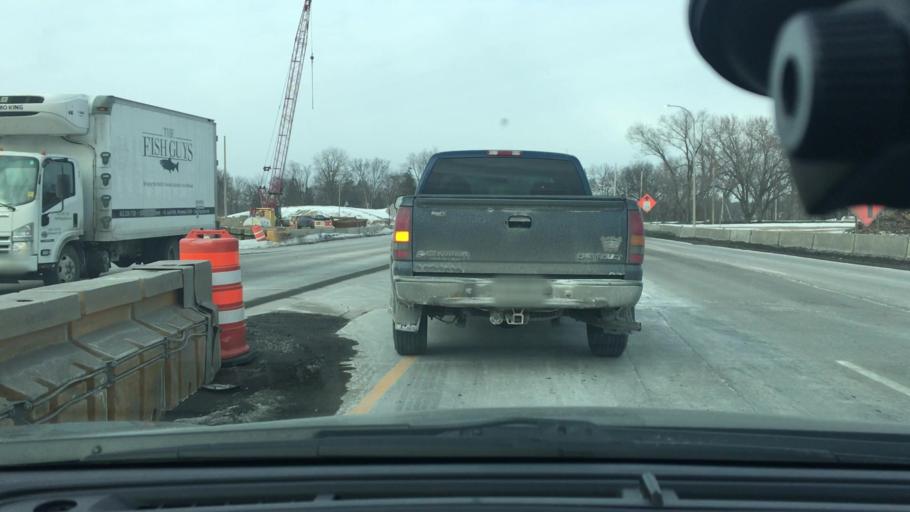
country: US
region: Minnesota
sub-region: Hennepin County
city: Champlin
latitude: 45.1846
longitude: -93.3921
